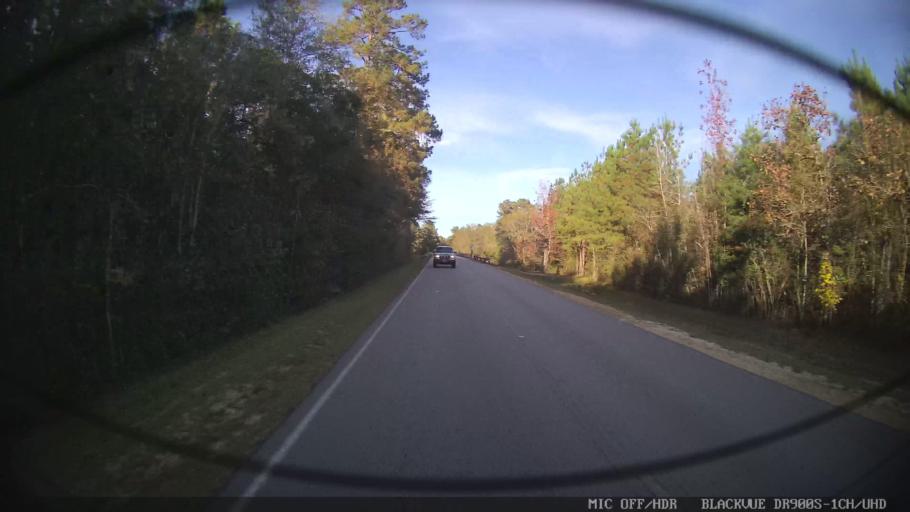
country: US
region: Mississippi
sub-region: Lamar County
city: Purvis
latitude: 31.1552
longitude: -89.3336
